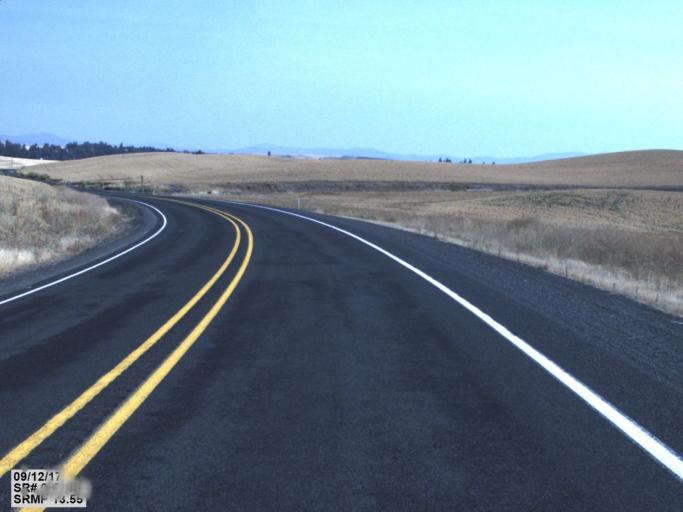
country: US
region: Washington
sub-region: Whitman County
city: Pullman
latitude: 46.8971
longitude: -117.0990
